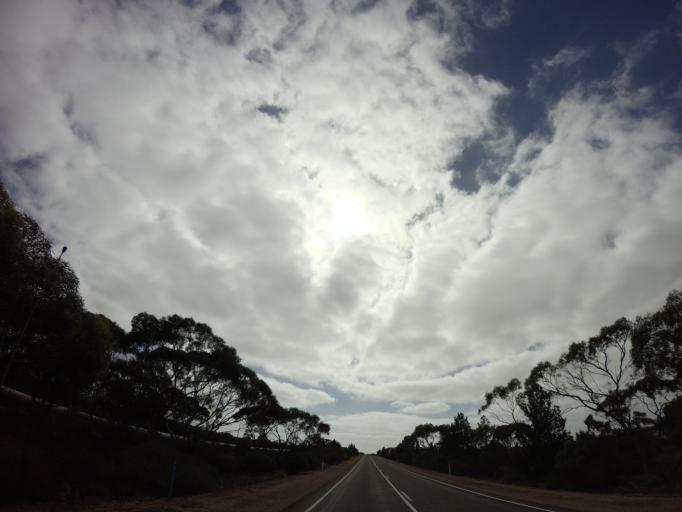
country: AU
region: South Australia
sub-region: Streaky Bay
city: Streaky Bay
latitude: -32.7242
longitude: 134.8527
